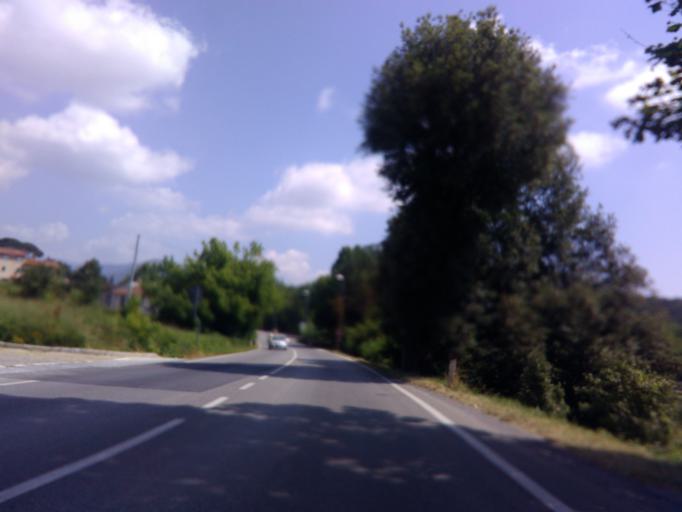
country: IT
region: Tuscany
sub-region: Provincia di Lucca
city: Porcari
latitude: 43.8664
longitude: 10.6358
